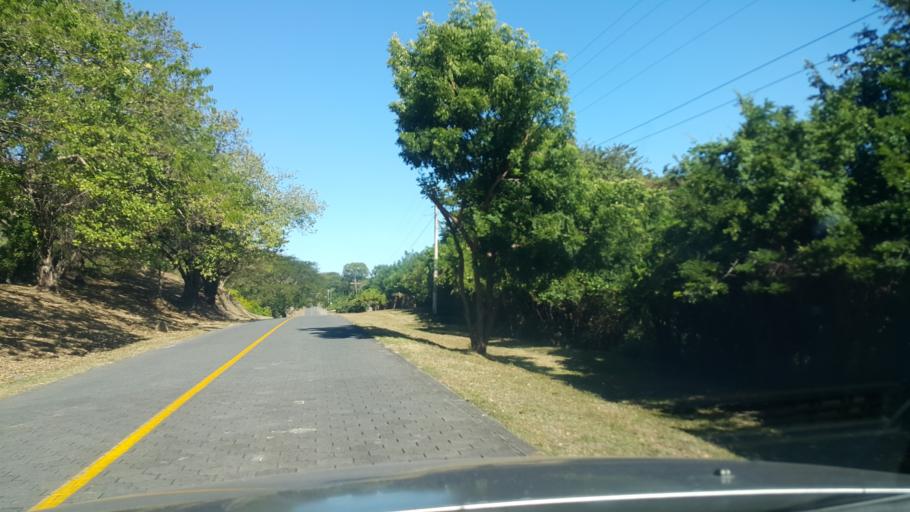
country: NI
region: Rivas
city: Moyogalpa
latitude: 11.4953
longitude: -85.6259
